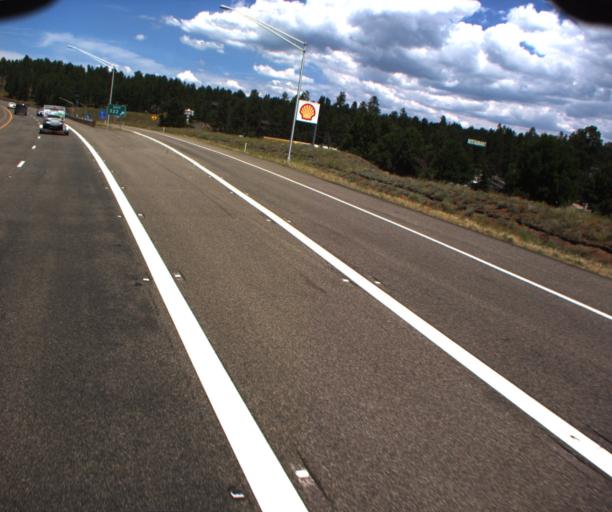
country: US
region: Arizona
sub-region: Coconino County
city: Sedona
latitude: 34.9395
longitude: -111.6507
